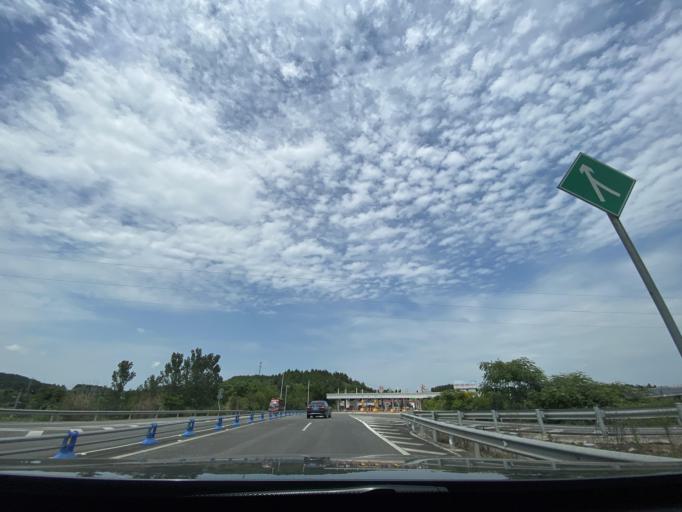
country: CN
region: Sichuan
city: Mianyang
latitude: 31.3516
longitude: 104.7092
